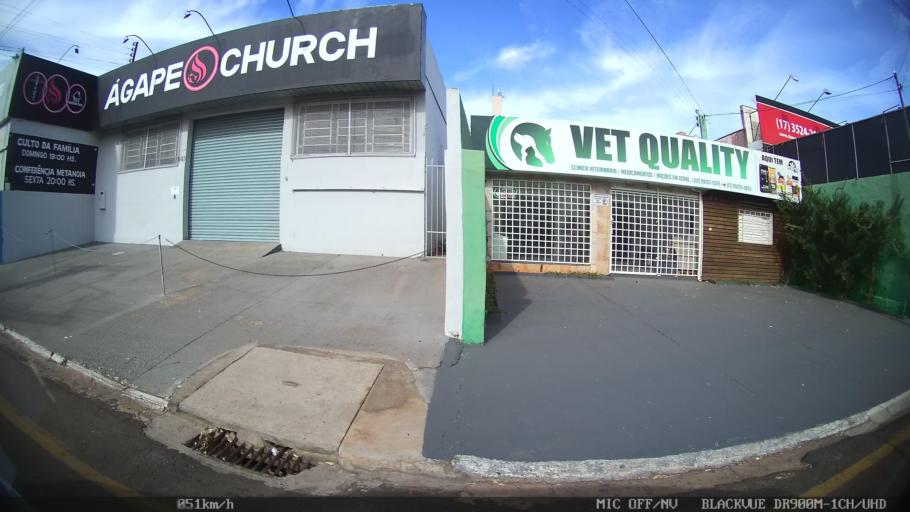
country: BR
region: Sao Paulo
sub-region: Catanduva
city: Catanduva
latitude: -21.1320
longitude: -48.9753
